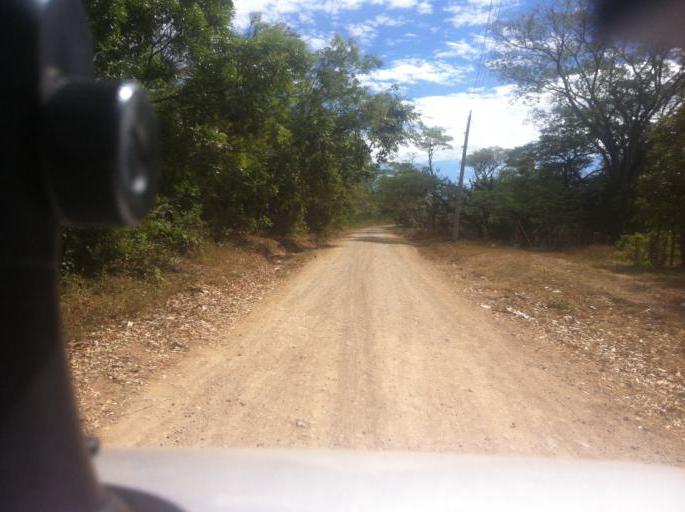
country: NI
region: Granada
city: Nandaime
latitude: 11.6035
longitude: -86.0293
